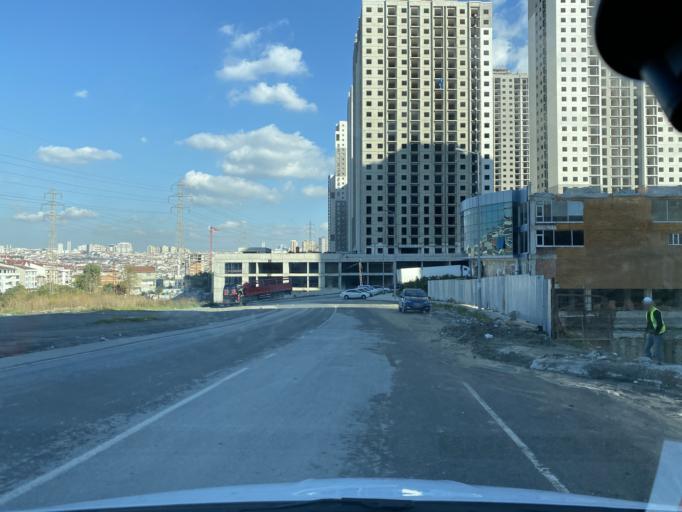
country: TR
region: Istanbul
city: Esenyurt
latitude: 41.0271
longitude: 28.6523
